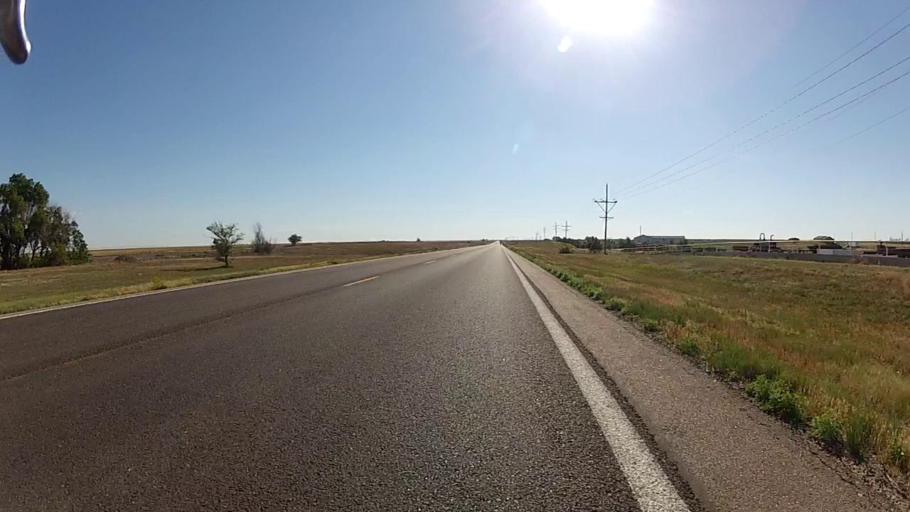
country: US
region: Kansas
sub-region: Haskell County
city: Sublette
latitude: 37.5467
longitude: -100.6153
